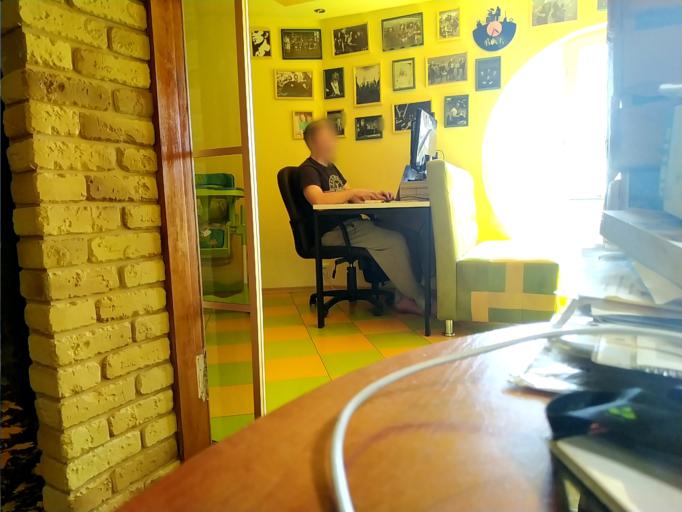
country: RU
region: Moskovskaya
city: Pavlovskiy Posad
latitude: 55.7436
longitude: 38.6660
